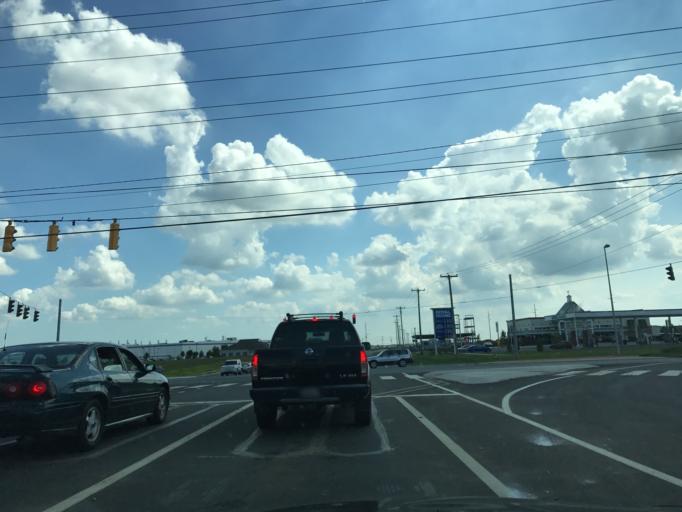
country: US
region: Delaware
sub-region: New Castle County
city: Middletown
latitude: 39.4410
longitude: -75.7473
